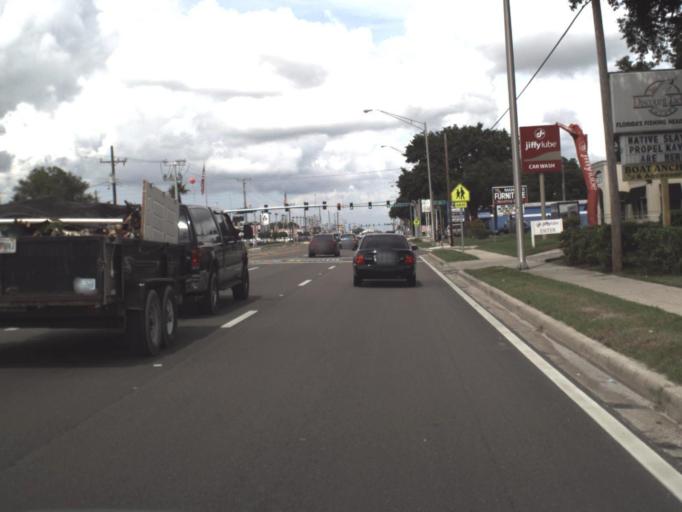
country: US
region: Florida
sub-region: Manatee County
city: West Samoset
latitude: 27.4718
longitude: -82.5629
